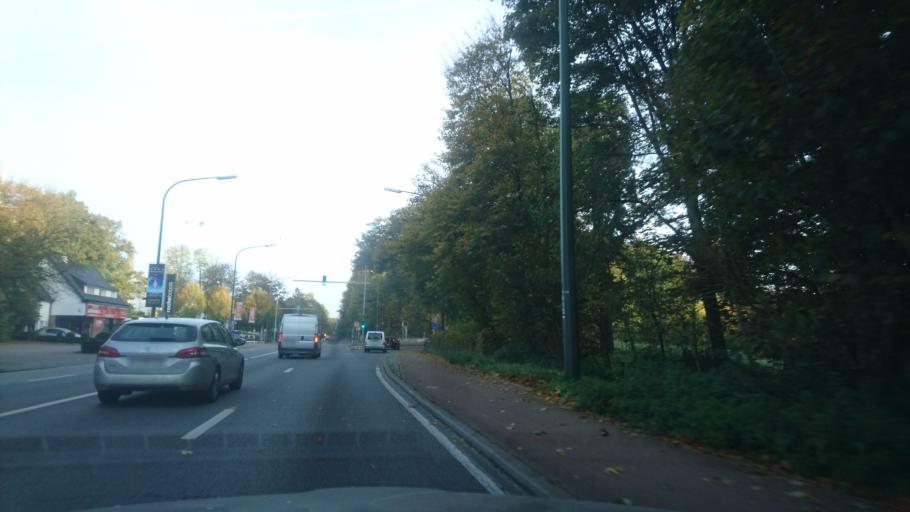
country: BE
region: Flanders
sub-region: Provincie Vlaams-Brabant
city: Sint-Genesius-Rode
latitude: 50.7688
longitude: 4.3827
